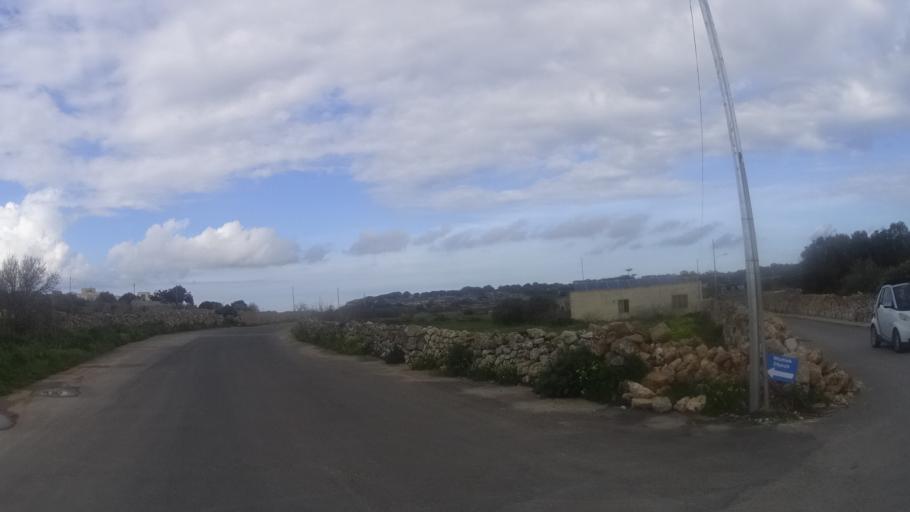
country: MT
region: L-Imtarfa
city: Imtarfa
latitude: 35.9005
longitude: 14.3787
